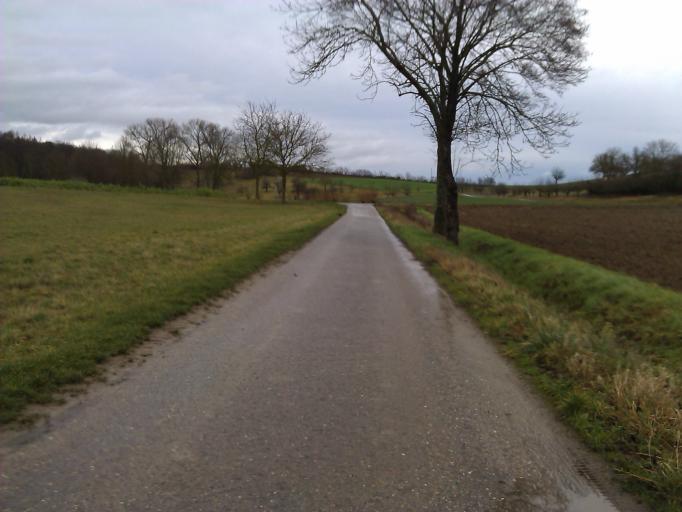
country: DE
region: Baden-Wuerttemberg
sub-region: Regierungsbezirk Stuttgart
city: Bad Wimpfen
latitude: 49.1978
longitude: 9.1570
